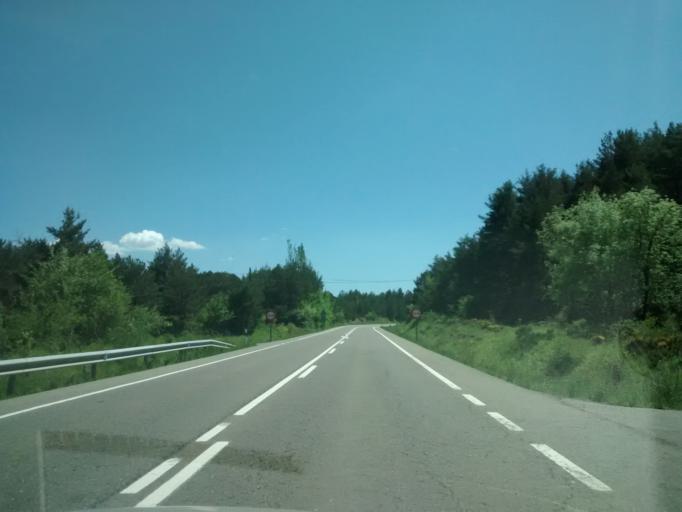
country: ES
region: Aragon
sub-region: Provincia de Huesca
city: Villanua
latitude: 42.6609
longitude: -0.5545
